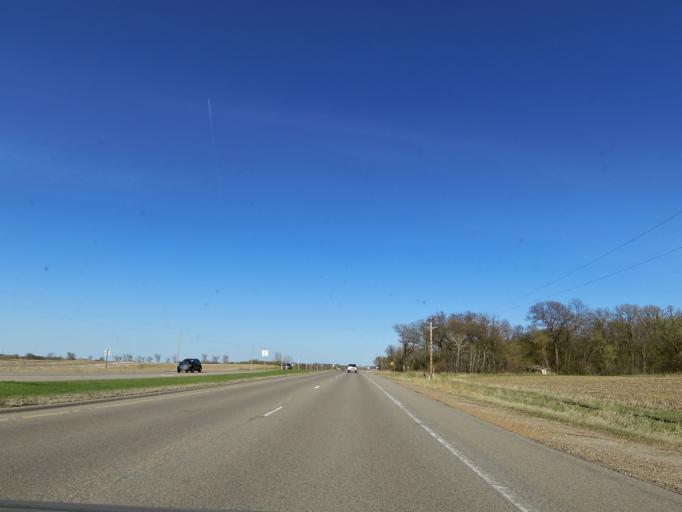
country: US
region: Minnesota
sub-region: Scott County
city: Elko New Market
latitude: 44.5731
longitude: -93.3233
